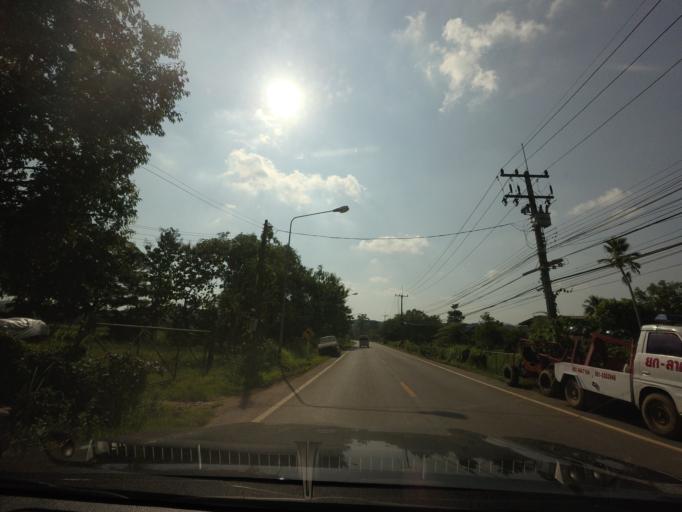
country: TH
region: Nan
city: Santi Suk
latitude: 18.9251
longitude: 100.9296
